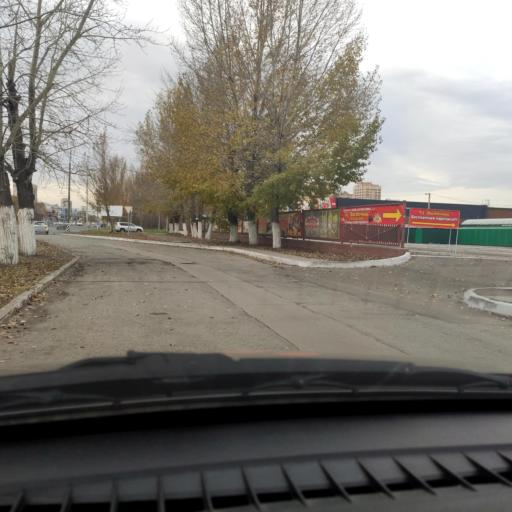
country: RU
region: Samara
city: Tol'yatti
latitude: 53.5406
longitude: 49.2841
